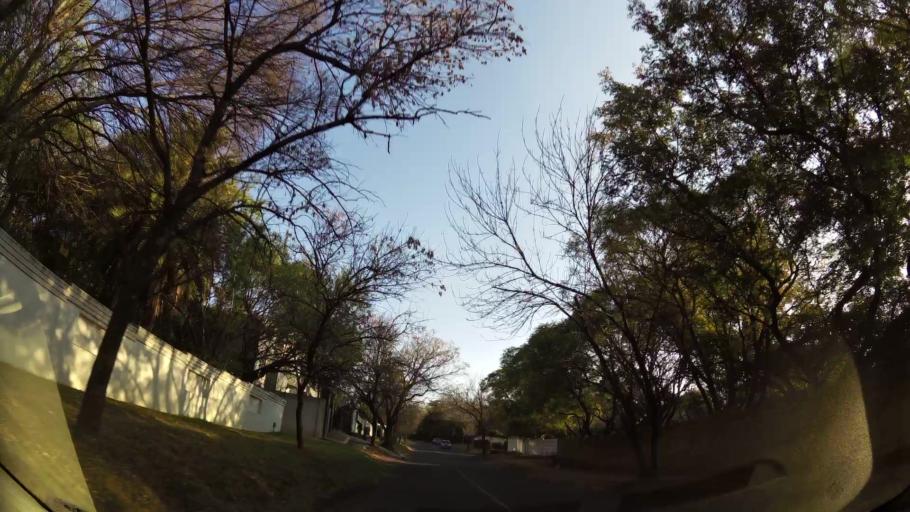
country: ZA
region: Gauteng
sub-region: City of Johannesburg Metropolitan Municipality
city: Diepsloot
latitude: -26.0703
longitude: 28.0005
